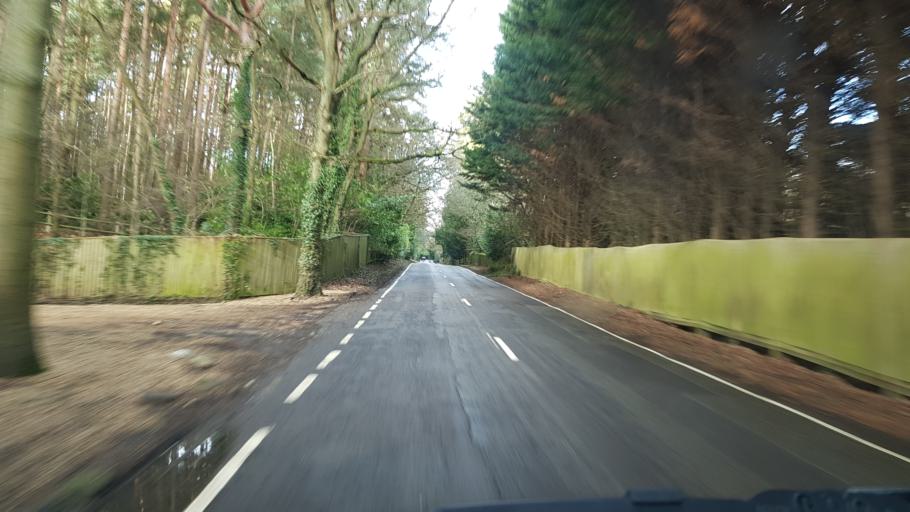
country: GB
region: England
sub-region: Surrey
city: Churt
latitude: 51.1668
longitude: -0.7491
